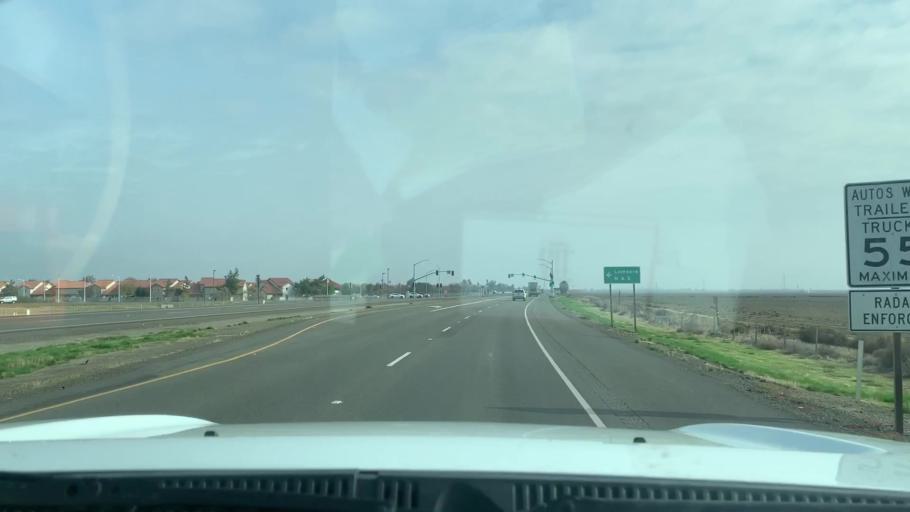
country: US
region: California
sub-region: Kings County
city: Lemoore Station
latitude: 36.2553
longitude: -119.8987
